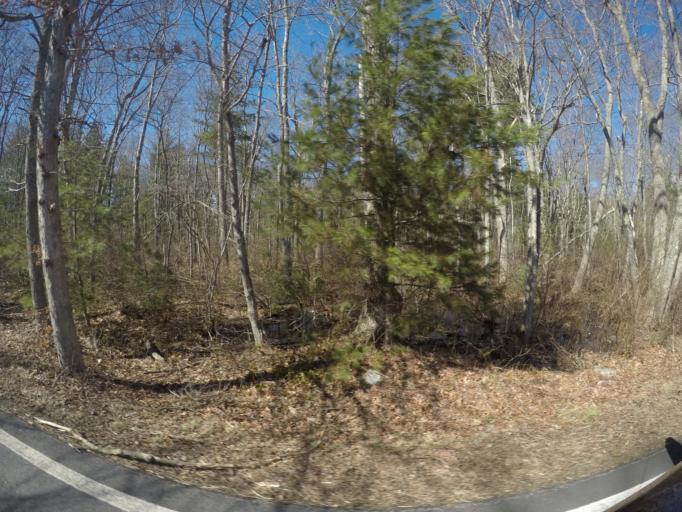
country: US
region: Massachusetts
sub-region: Bristol County
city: Easton
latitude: 42.0084
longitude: -71.1142
